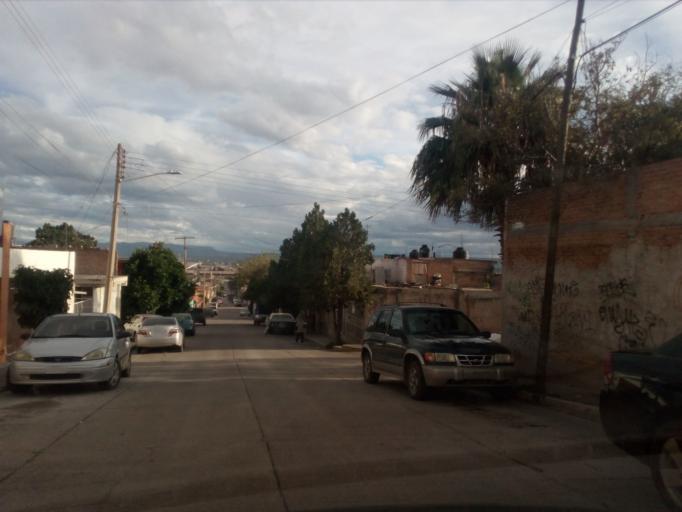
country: MX
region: Durango
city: Victoria de Durango
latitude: 24.0441
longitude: -104.6659
